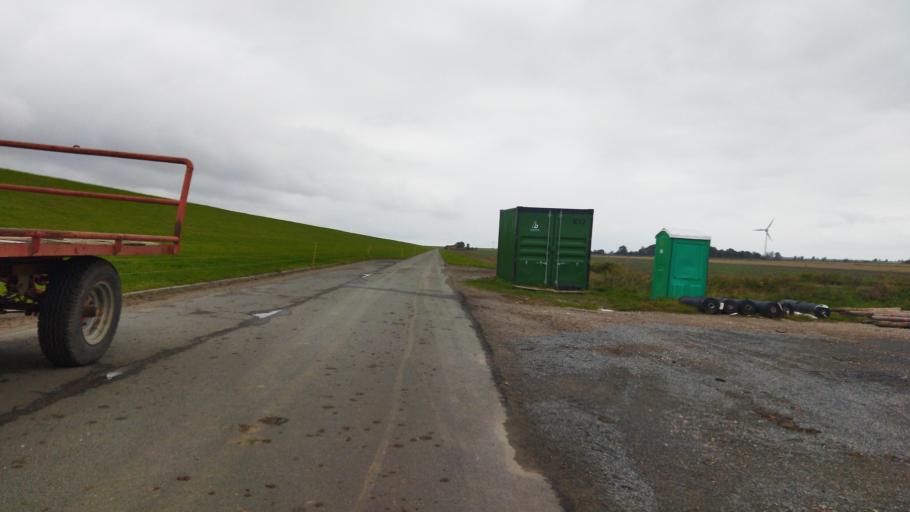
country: NL
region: Groningen
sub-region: Gemeente Delfzijl
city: Delfzijl
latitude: 53.4471
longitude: 7.0216
